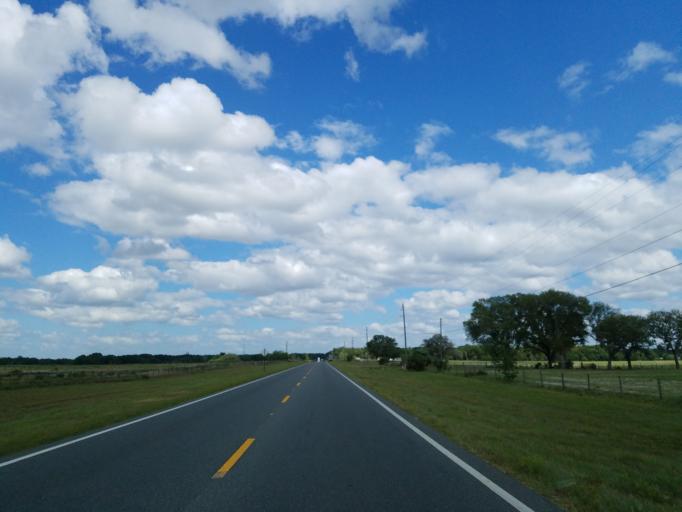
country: US
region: Florida
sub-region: Sumter County
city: Lake Panasoffkee
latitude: 28.7488
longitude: -82.0825
